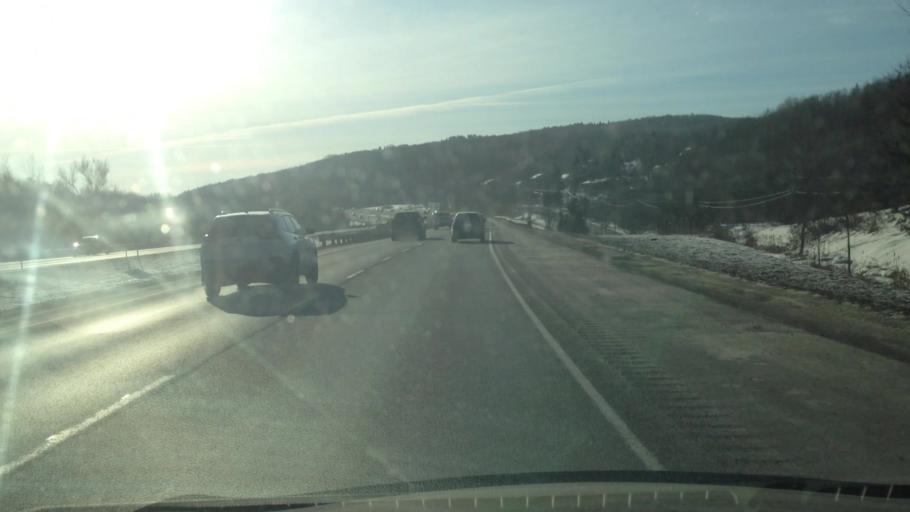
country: CA
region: Quebec
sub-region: Laurentides
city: Prevost
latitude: 45.8710
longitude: -74.0868
